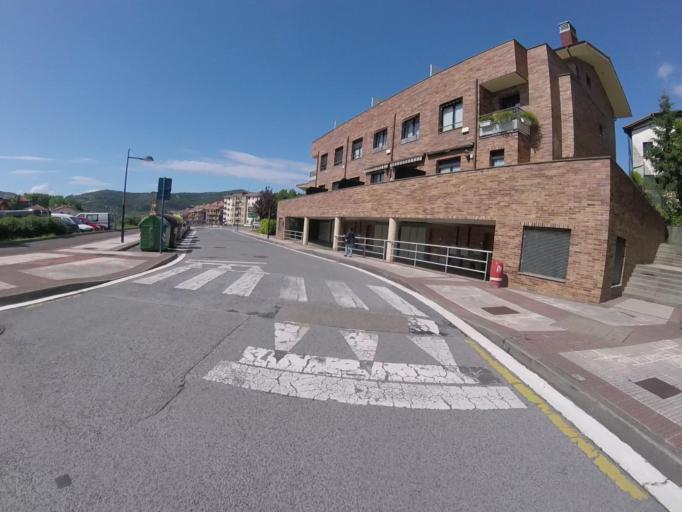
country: ES
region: Basque Country
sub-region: Provincia de Guipuzcoa
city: Errenteria
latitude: 43.3092
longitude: -1.8970
